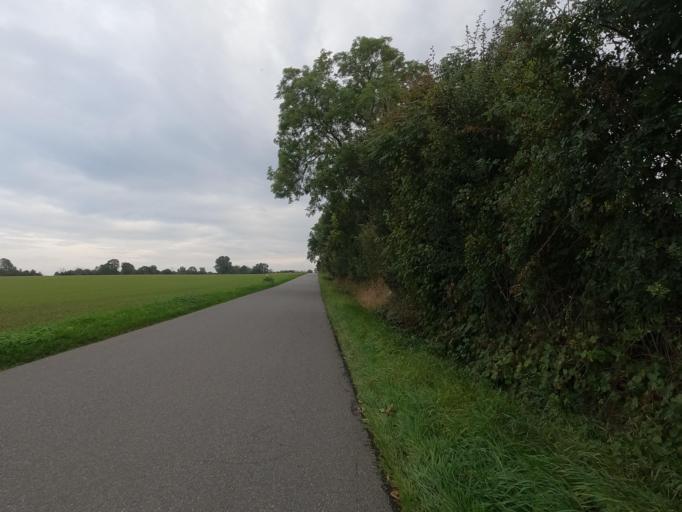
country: DE
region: Schleswig-Holstein
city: Neukirchen
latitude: 54.3087
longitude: 11.0432
